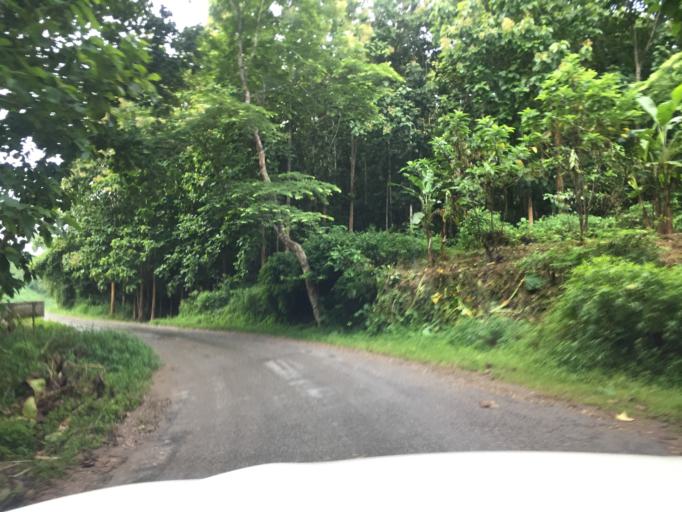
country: LA
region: Oudomxai
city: Muang La
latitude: 21.0388
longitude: 102.2401
